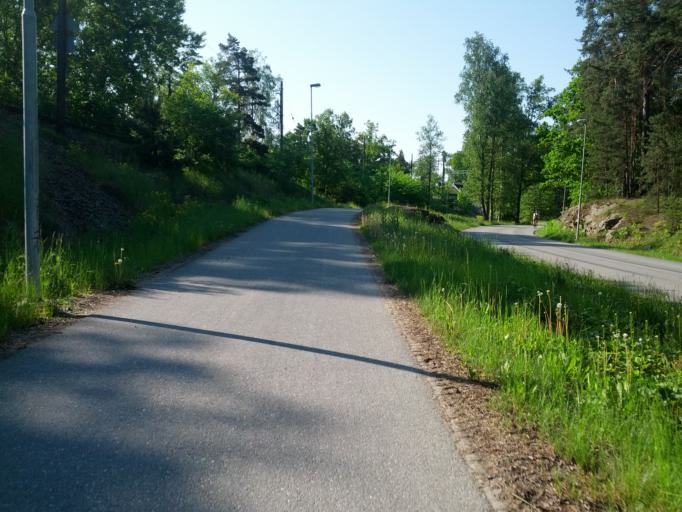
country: SE
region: Stockholm
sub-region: Danderyds Kommun
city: Djursholm
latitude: 59.4072
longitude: 18.0603
